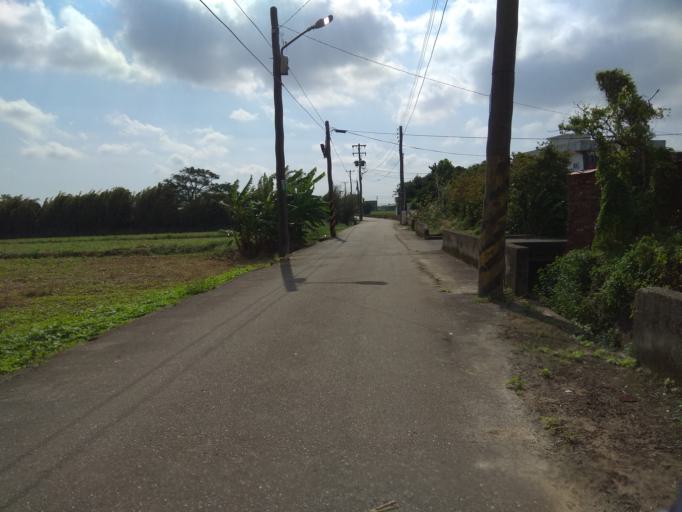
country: TW
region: Taiwan
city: Taoyuan City
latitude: 25.0754
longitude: 121.2489
